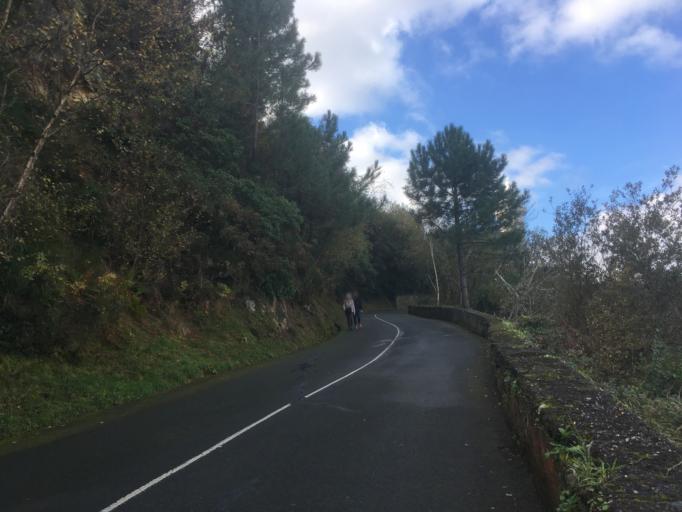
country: ES
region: Basque Country
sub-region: Provincia de Guipuzcoa
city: San Sebastian
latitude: 43.3227
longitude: -2.0091
